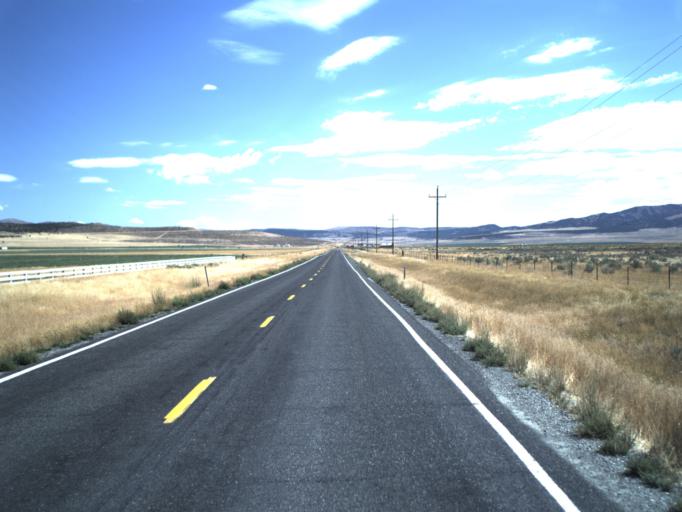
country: US
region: Idaho
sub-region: Oneida County
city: Malad City
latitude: 41.9672
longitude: -112.8030
